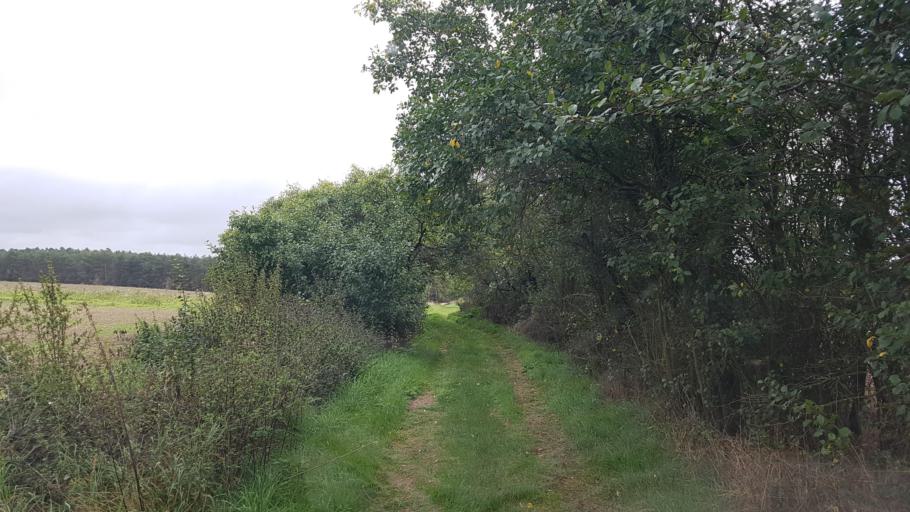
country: DE
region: Brandenburg
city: Hohenbucko
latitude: 51.6949
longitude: 13.5002
